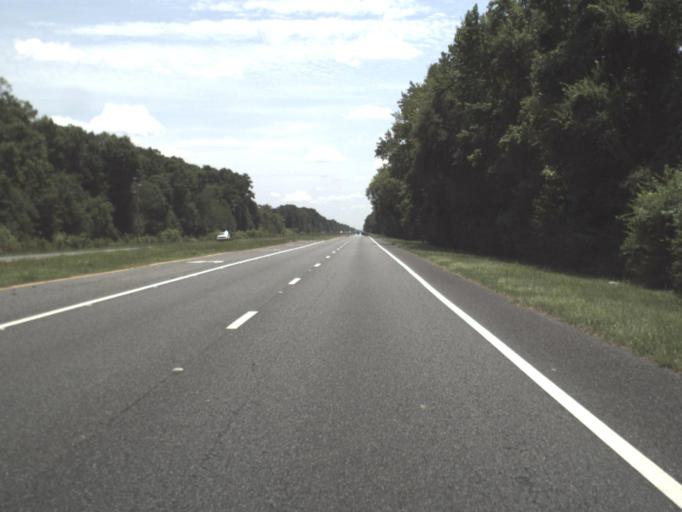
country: US
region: Florida
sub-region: Dixie County
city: Cross City
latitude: 29.6765
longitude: -83.2471
